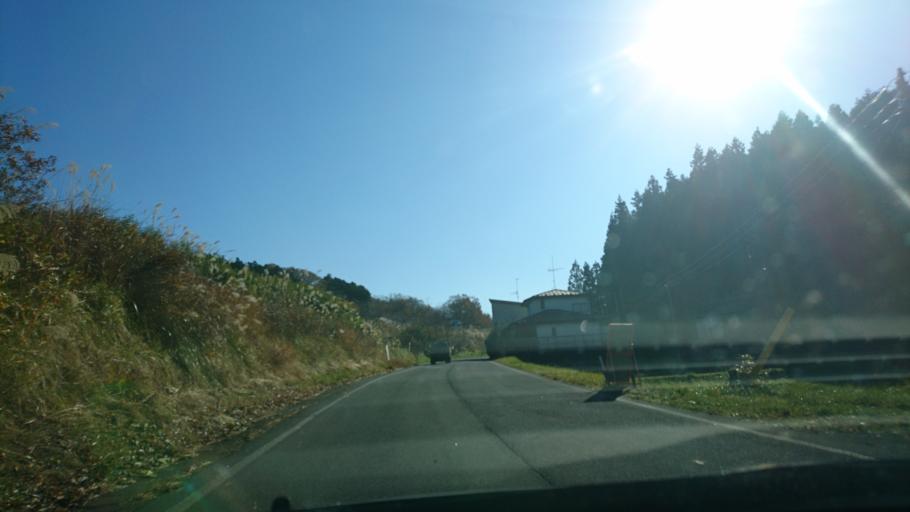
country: JP
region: Iwate
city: Ichinoseki
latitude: 39.0014
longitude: 141.2660
